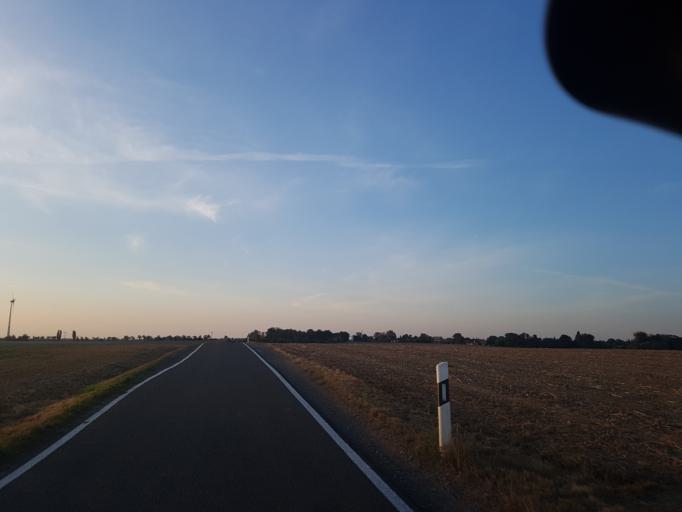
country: DE
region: Saxony
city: Stauchitz
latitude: 51.2971
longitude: 13.1902
